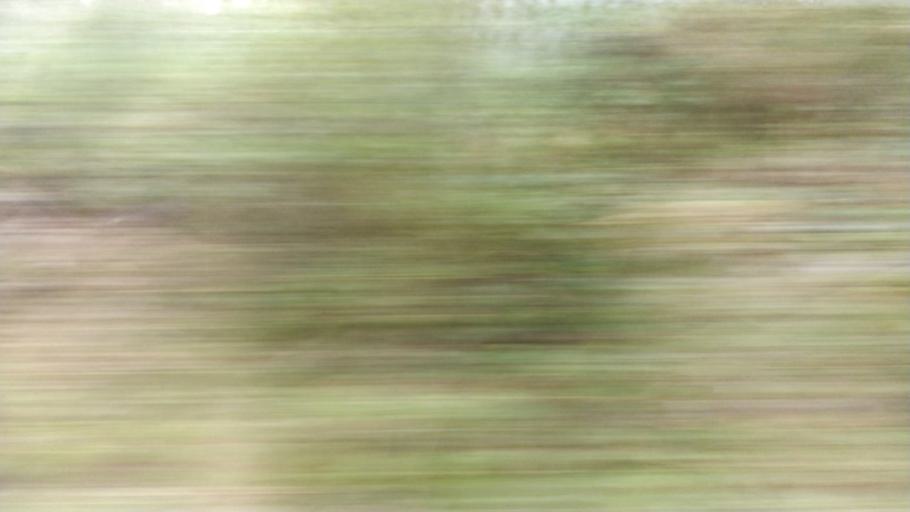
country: GB
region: England
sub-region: Lancashire
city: Appley Bridge
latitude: 53.5846
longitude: -2.7440
